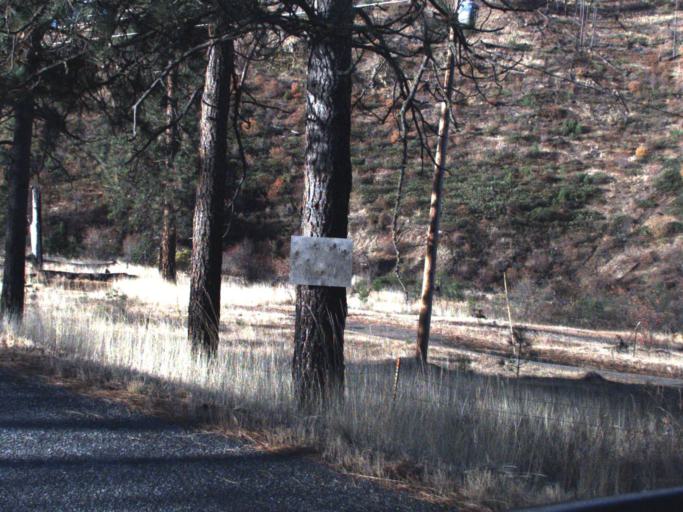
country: US
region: Washington
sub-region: Okanogan County
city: Coulee Dam
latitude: 48.0866
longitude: -118.6933
